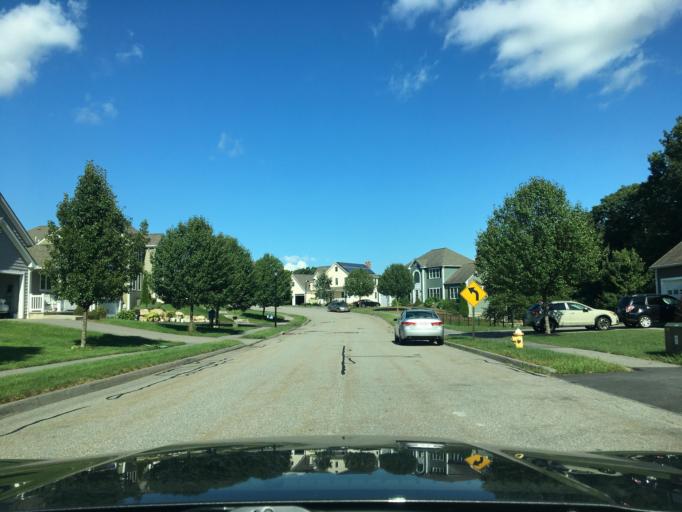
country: US
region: Massachusetts
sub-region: Worcester County
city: Holden
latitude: 42.3178
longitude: -71.8296
